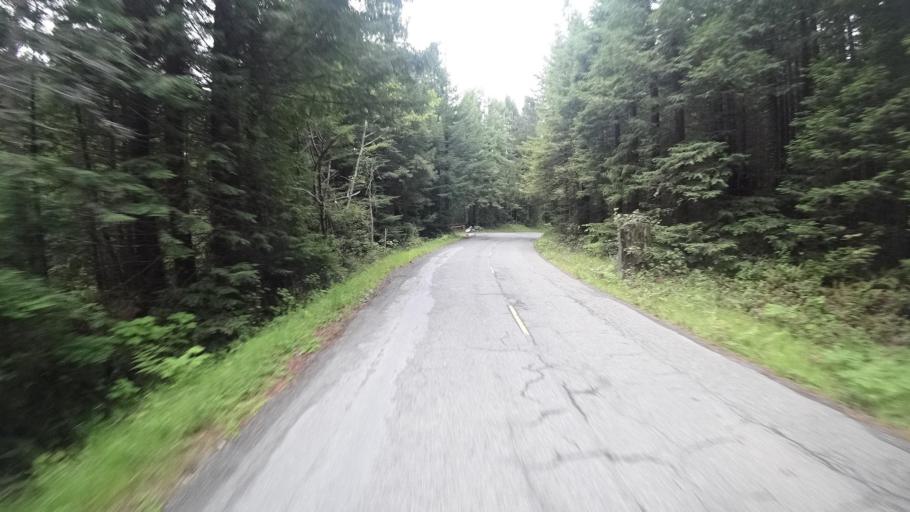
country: US
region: California
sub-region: Humboldt County
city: Blue Lake
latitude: 40.8730
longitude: -123.9690
